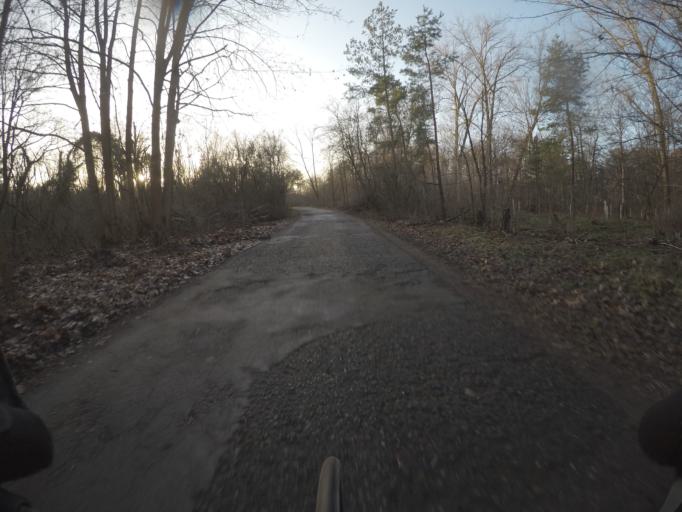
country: DE
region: Brandenburg
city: Hennigsdorf
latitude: 52.6613
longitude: 13.2266
